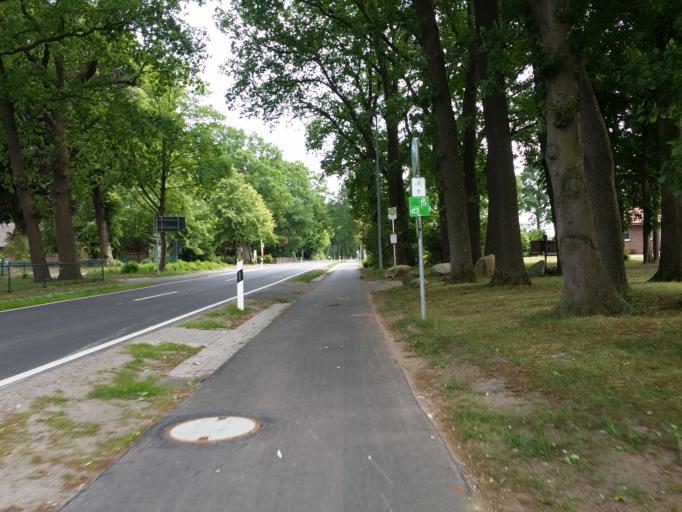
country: DE
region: Lower Saxony
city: Rastede
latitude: 53.2127
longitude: 8.1971
